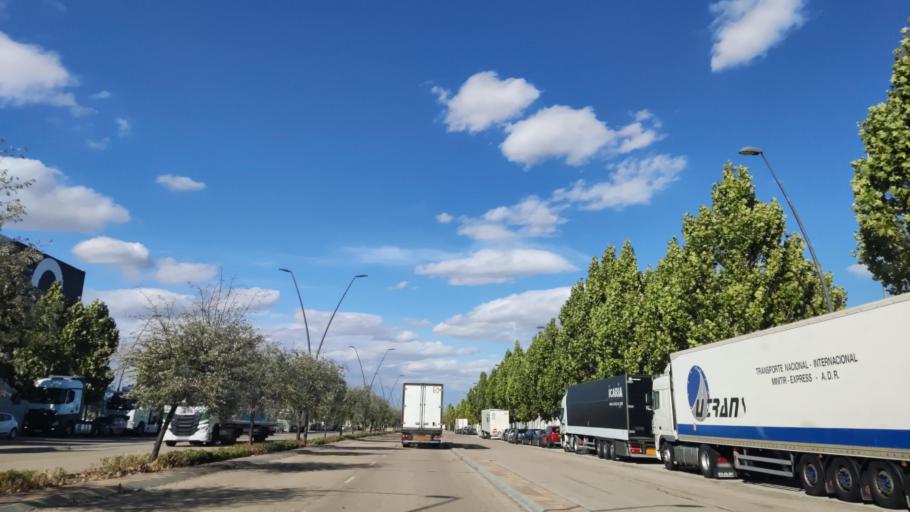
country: ES
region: Madrid
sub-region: Provincia de Madrid
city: Pinto
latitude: 40.2806
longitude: -3.6813
